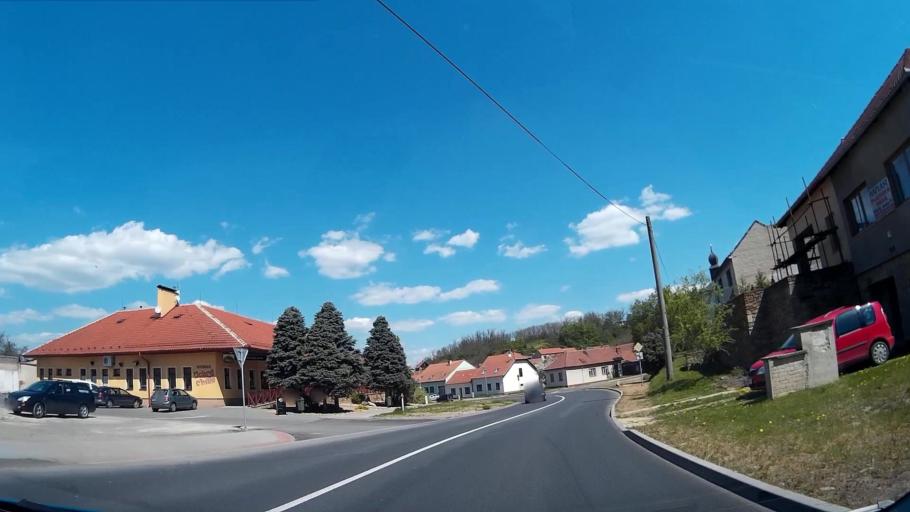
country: CZ
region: South Moravian
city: Ivancice
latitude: 49.1405
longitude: 16.3886
